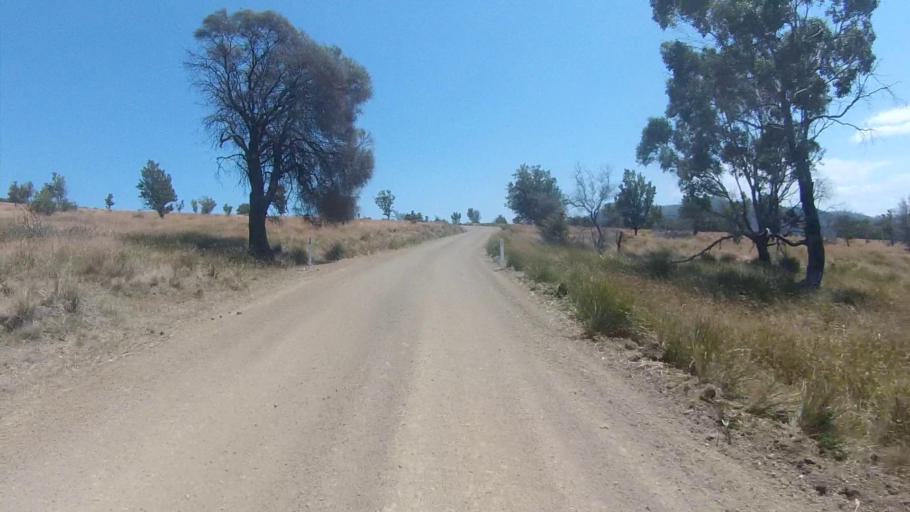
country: AU
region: Tasmania
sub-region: Sorell
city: Sorell
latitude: -42.8966
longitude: 147.8358
